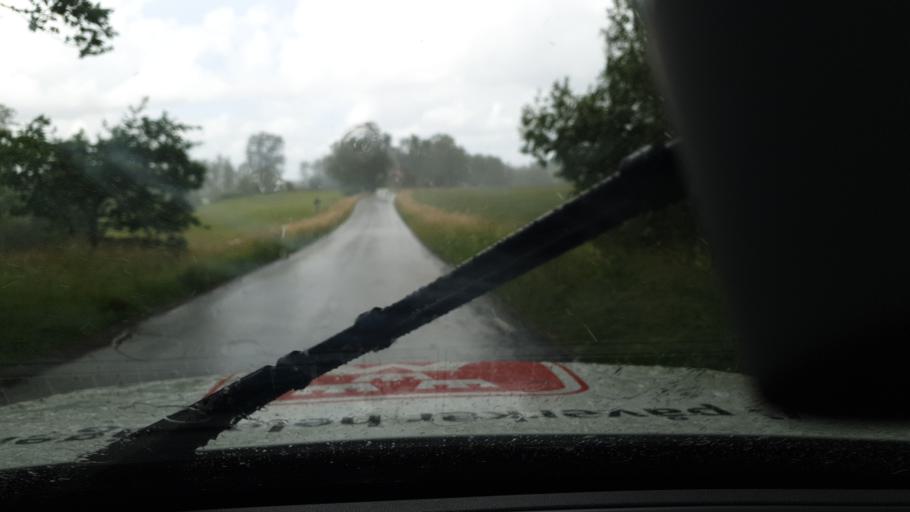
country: SE
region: Vaestra Goetaland
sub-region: Falkopings Kommun
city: Akarp
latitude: 58.2369
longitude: 13.6016
